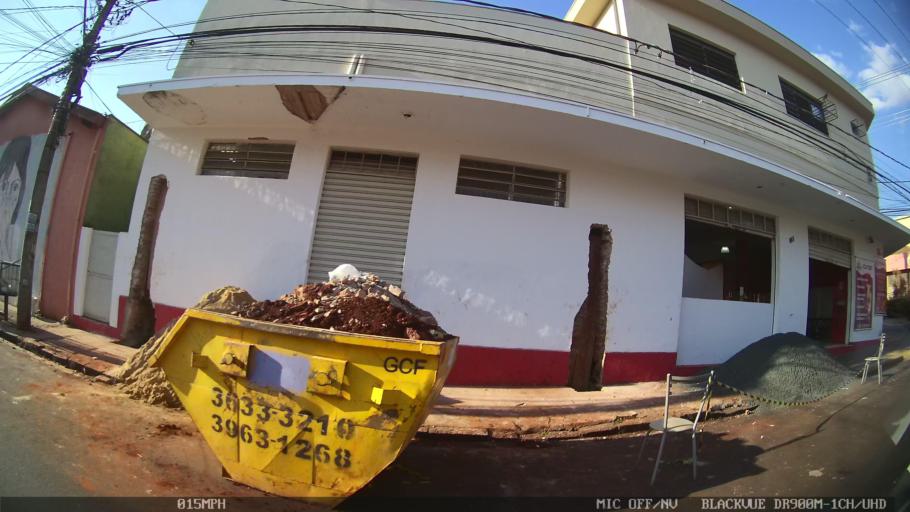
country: BR
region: Sao Paulo
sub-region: Ribeirao Preto
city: Ribeirao Preto
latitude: -21.1799
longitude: -47.7969
